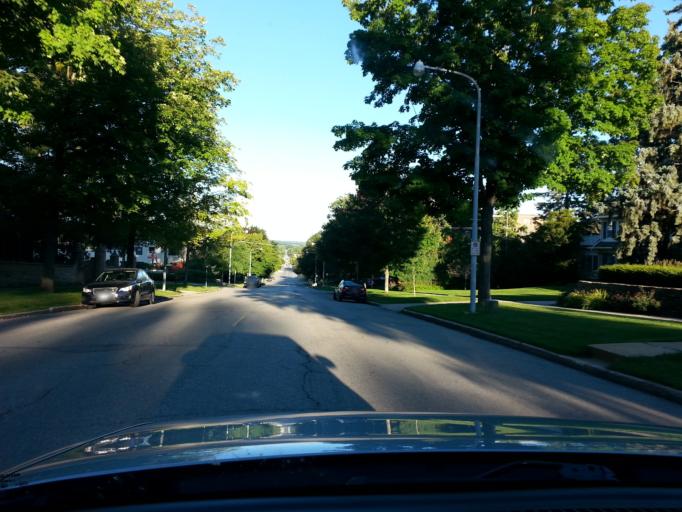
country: US
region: Minnesota
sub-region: Olmsted County
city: Rochester
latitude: 44.0193
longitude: -92.4740
